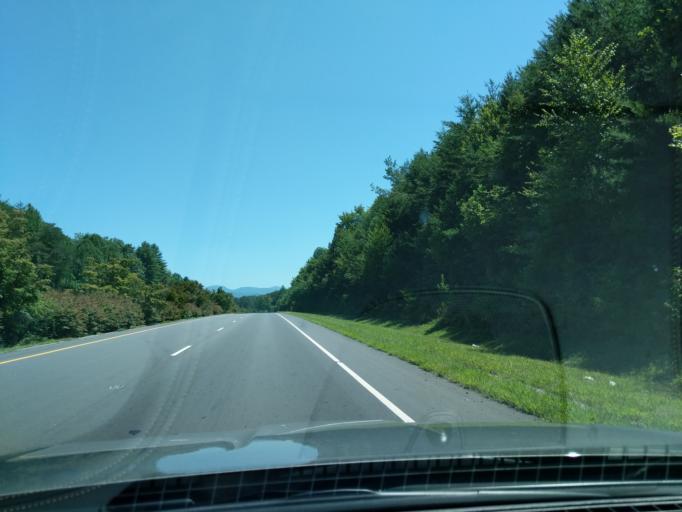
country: US
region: North Carolina
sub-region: Macon County
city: Franklin
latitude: 35.1645
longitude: -83.4221
